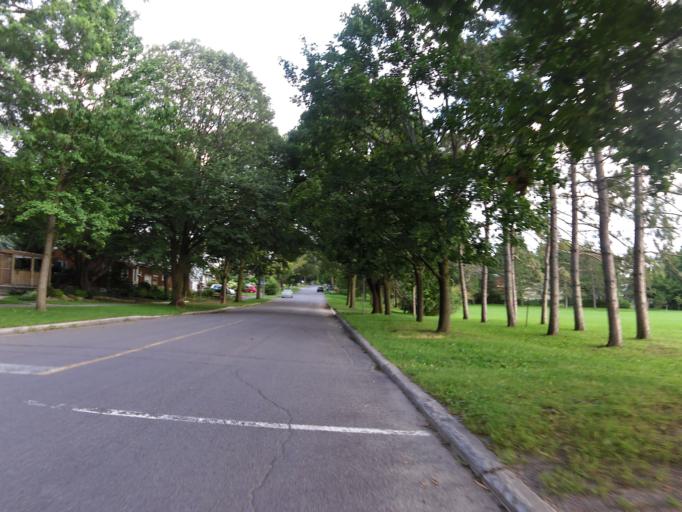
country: CA
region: Ontario
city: Ottawa
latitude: 45.3834
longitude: -75.7647
